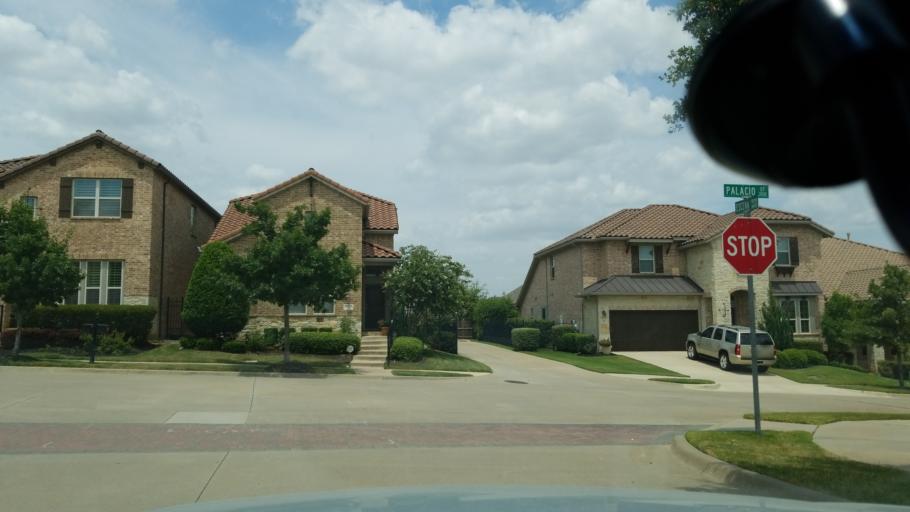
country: US
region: Texas
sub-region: Dallas County
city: Farmers Branch
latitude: 32.8999
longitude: -96.9428
